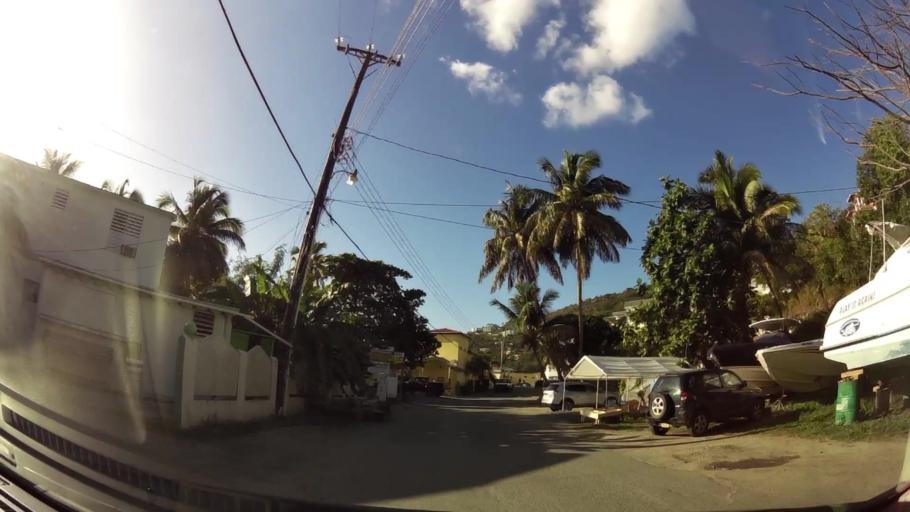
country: VG
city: Road Town
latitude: 18.4273
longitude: -64.6568
